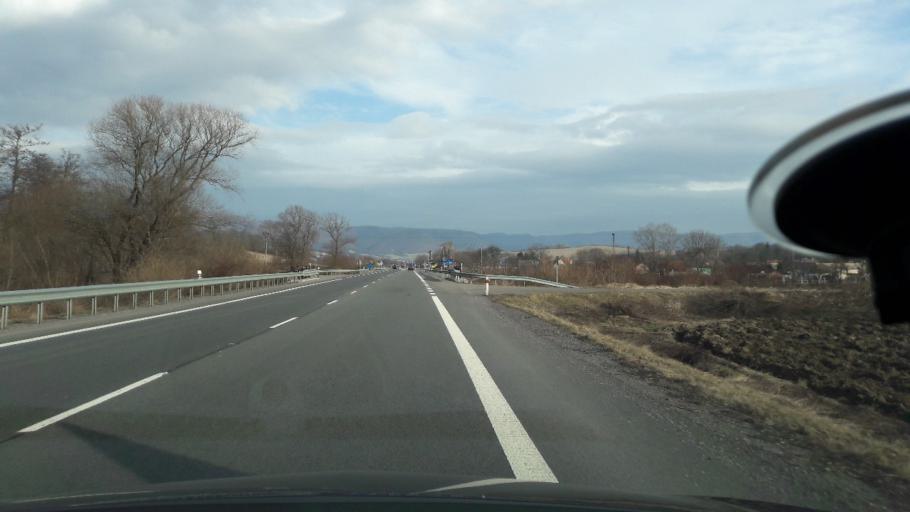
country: SK
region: Nitriansky
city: Prievidza
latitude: 48.7807
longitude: 18.6897
